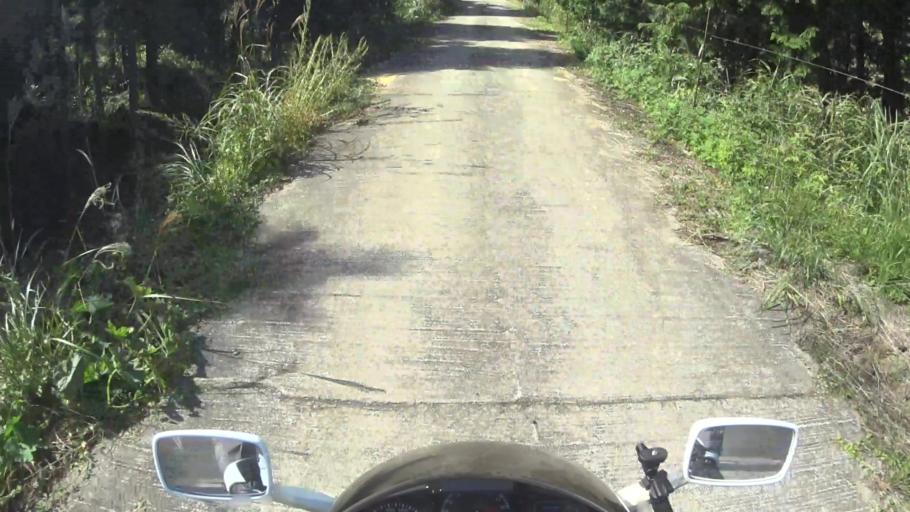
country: JP
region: Hyogo
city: Toyooka
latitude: 35.5620
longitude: 134.9175
